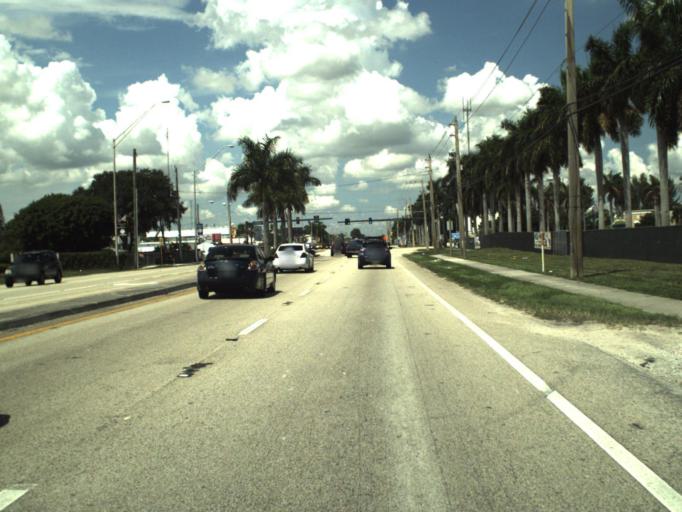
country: US
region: Florida
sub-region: Broward County
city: Pembroke Park
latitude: 25.9848
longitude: -80.1733
